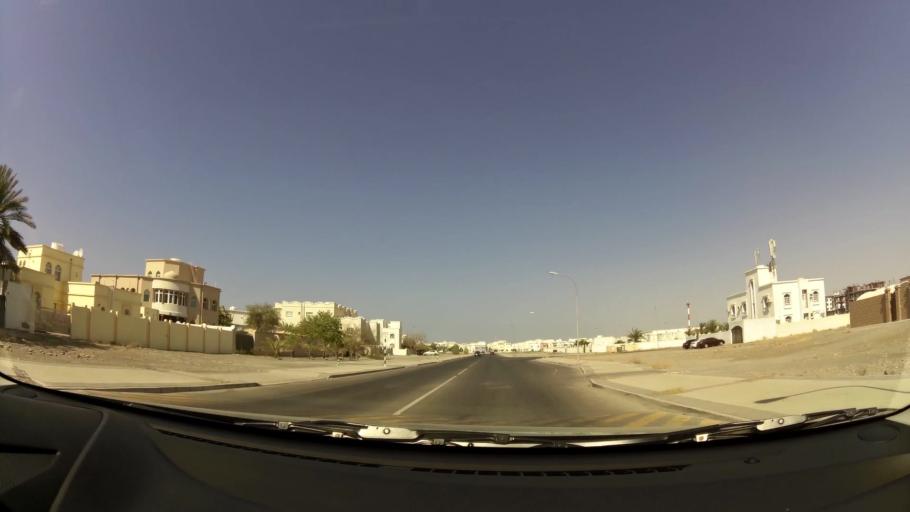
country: OM
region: Muhafazat Masqat
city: As Sib al Jadidah
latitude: 23.6226
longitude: 58.2090
